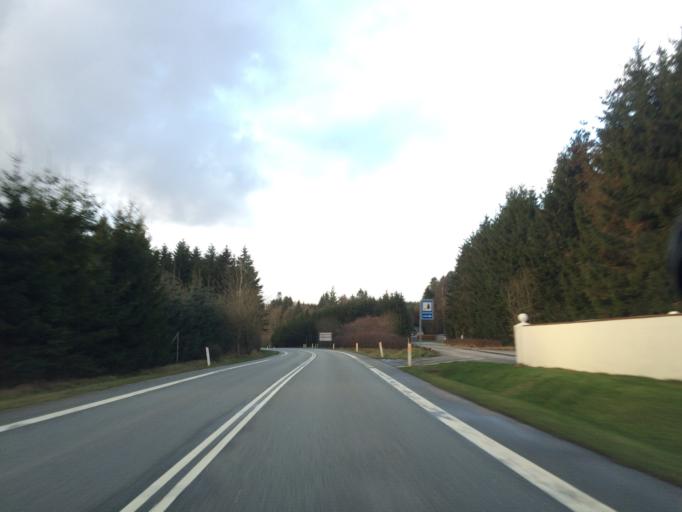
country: DK
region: Central Jutland
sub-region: Silkeborg Kommune
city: Svejbaek
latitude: 56.0969
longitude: 9.6486
